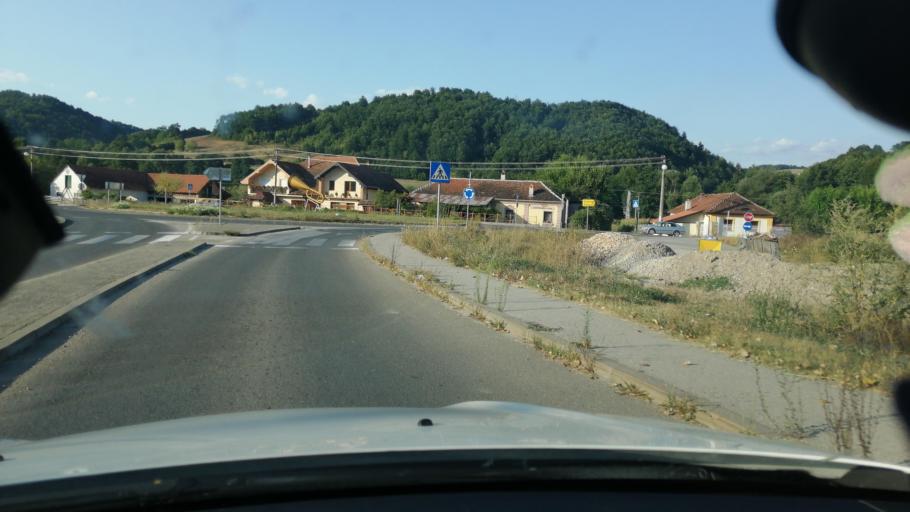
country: RS
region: Central Serbia
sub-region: Moravicki Okrug
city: Lucani
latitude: 43.7535
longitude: 20.2556
